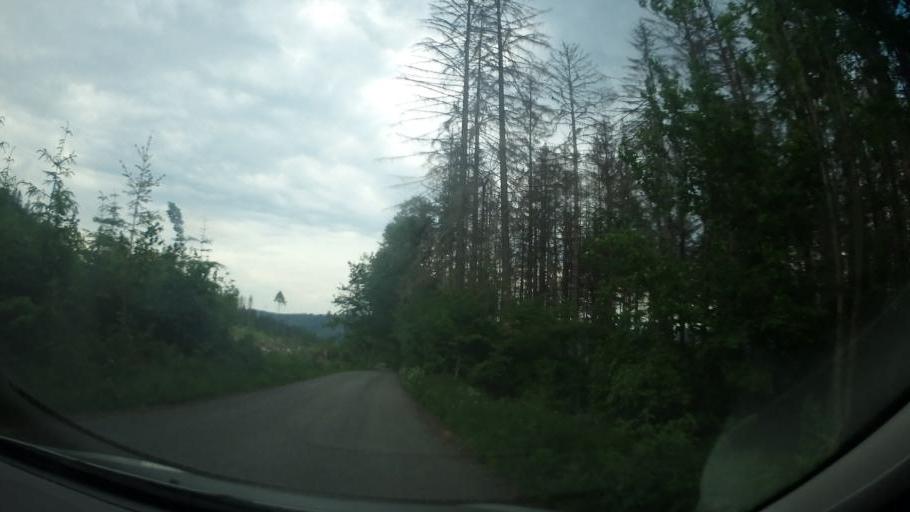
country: CZ
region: South Moravian
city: Olesnice
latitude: 49.4915
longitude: 16.4124
